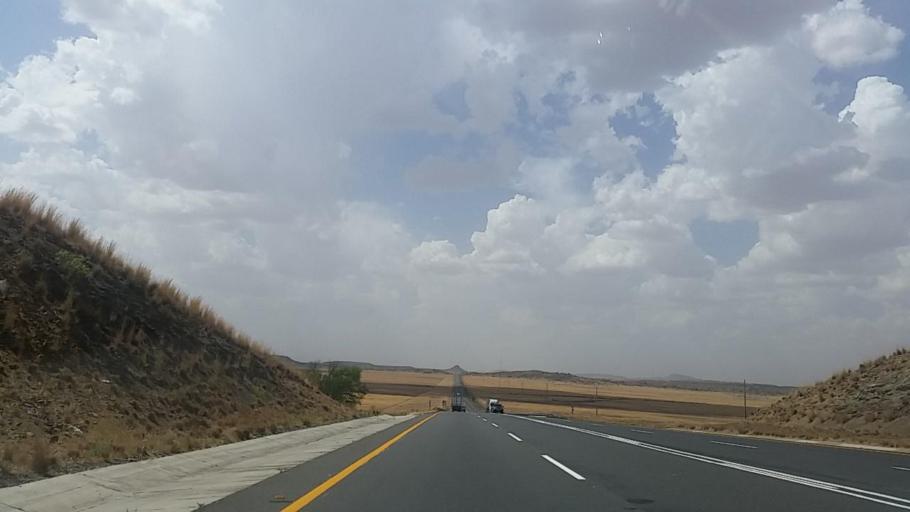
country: ZA
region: Orange Free State
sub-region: Xhariep District Municipality
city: Trompsburg
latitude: -30.3987
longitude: 25.6720
